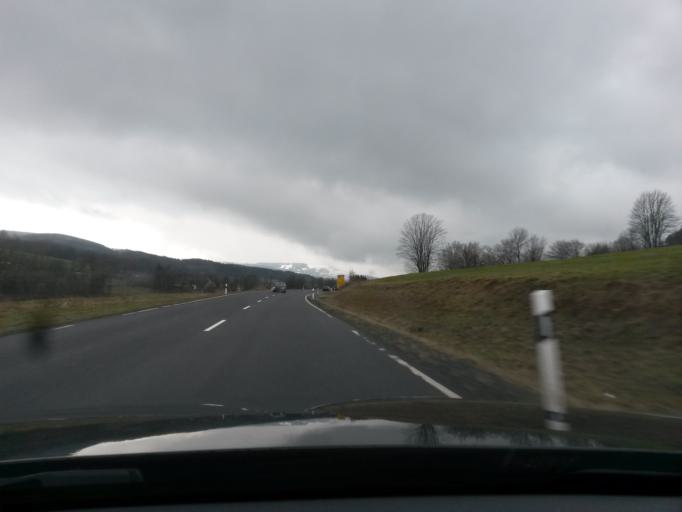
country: DE
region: Hesse
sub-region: Regierungsbezirk Kassel
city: Hilders
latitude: 50.5478
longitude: 9.9970
